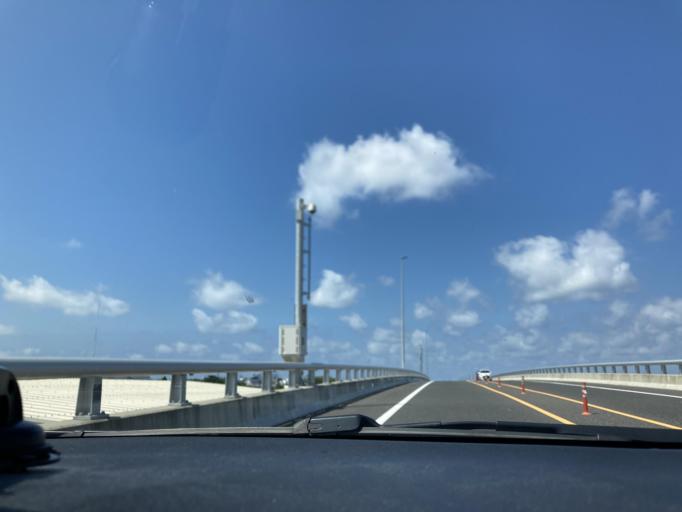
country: JP
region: Okinawa
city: Ginowan
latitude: 26.2741
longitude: 127.7115
